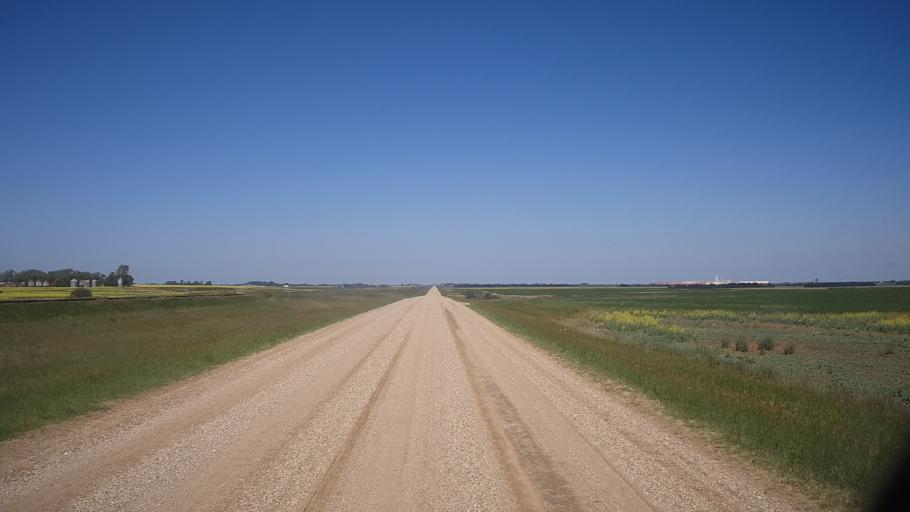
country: CA
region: Saskatchewan
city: Watrous
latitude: 51.8666
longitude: -105.9809
